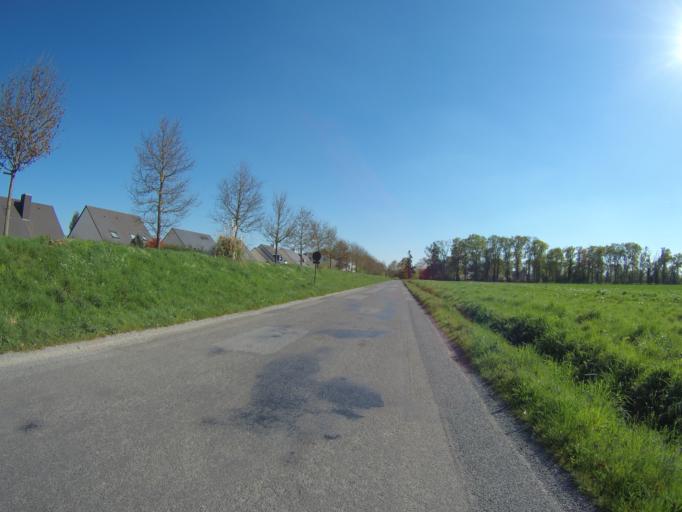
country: FR
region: Brittany
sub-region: Departement d'Ille-et-Vilaine
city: Vern-sur-Seiche
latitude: 48.0534
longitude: -1.6168
